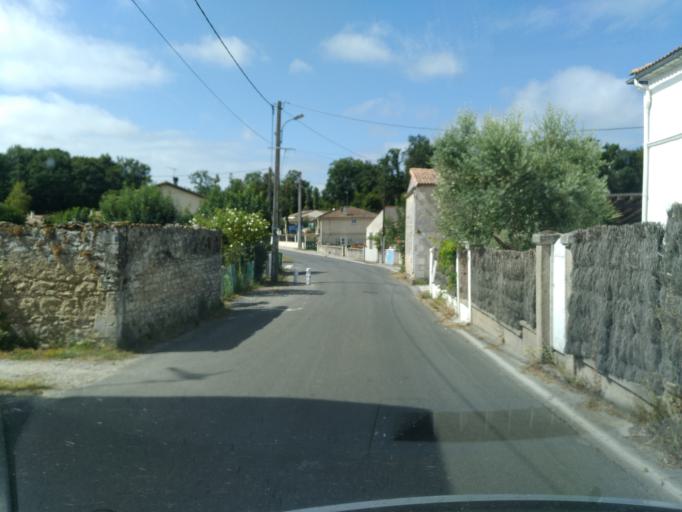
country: FR
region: Poitou-Charentes
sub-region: Departement de la Charente-Maritime
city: Breuillet
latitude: 45.6946
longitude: -1.0688
